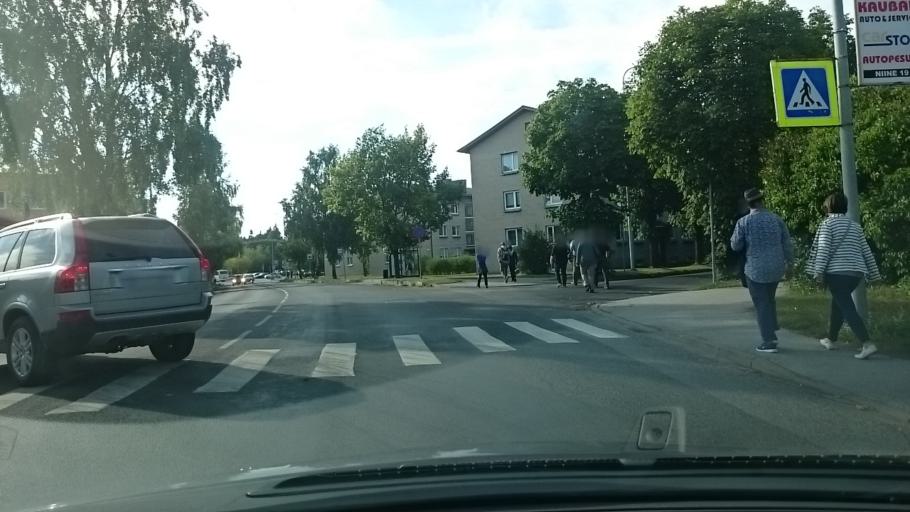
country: EE
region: Laeaene
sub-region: Haapsalu linn
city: Haapsalu
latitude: 58.9390
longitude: 23.5458
